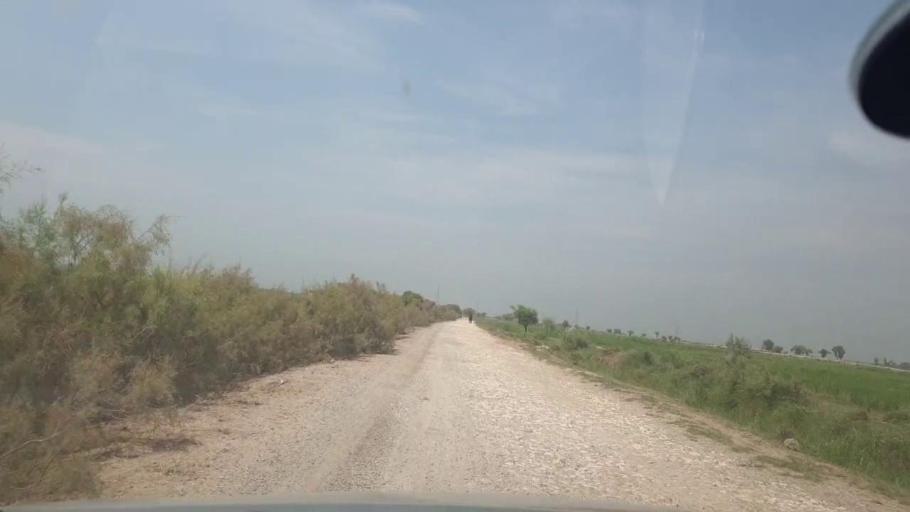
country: PK
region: Sindh
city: Thul
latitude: 28.1752
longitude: 68.6251
